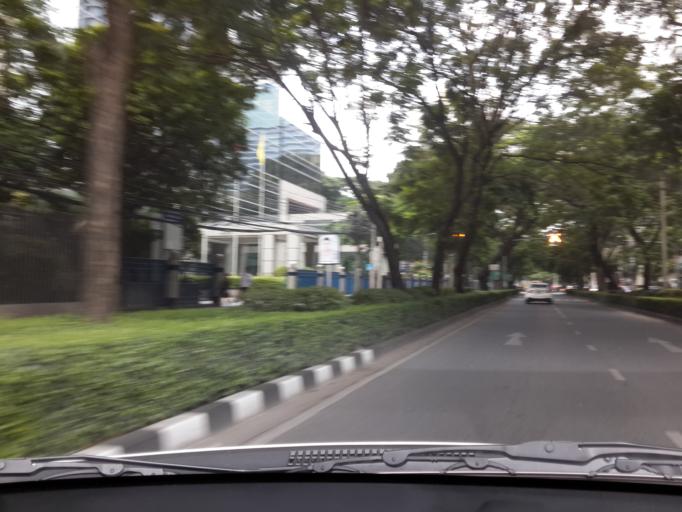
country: TH
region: Bangkok
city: Pathum Wan
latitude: 13.7387
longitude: 100.5467
